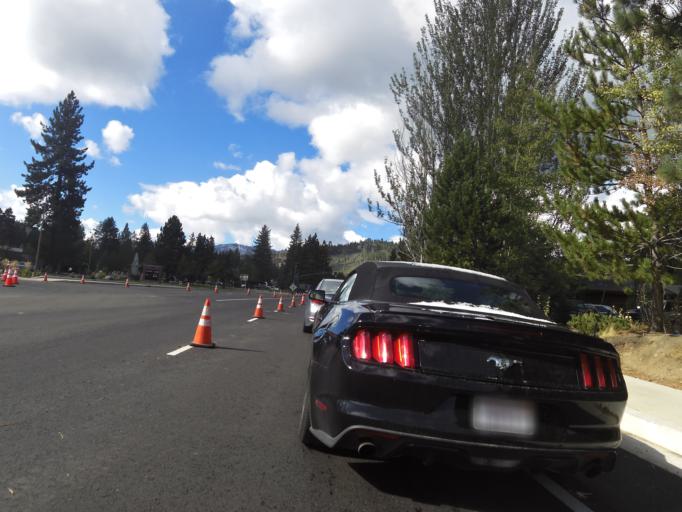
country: US
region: California
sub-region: El Dorado County
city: South Lake Tahoe
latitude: 38.9143
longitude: -120.0030
